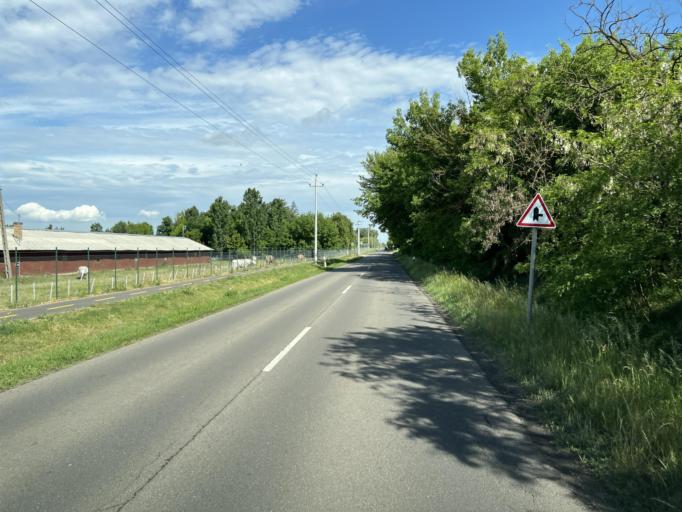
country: HU
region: Pest
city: Godollo
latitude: 47.5689
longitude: 19.3716
